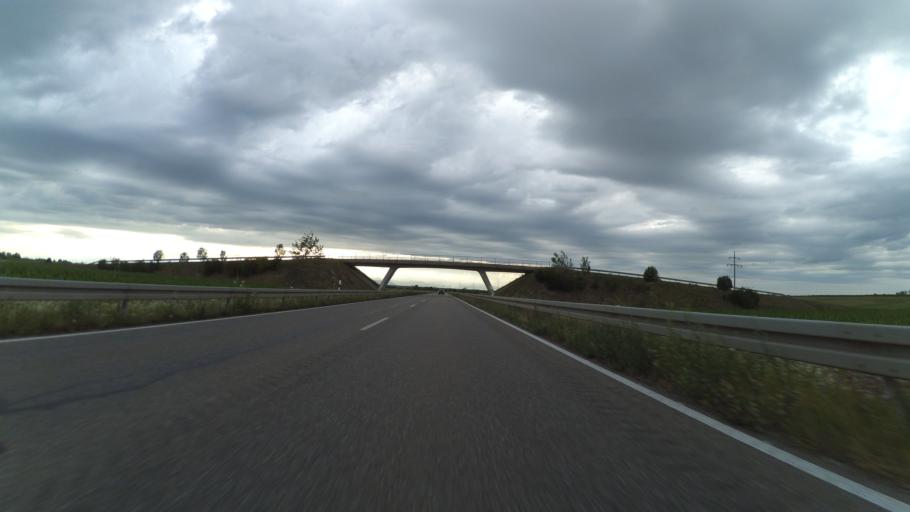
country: DE
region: Baden-Wuerttemberg
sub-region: Freiburg Region
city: Bad Krozingen
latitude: 47.9005
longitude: 7.6935
